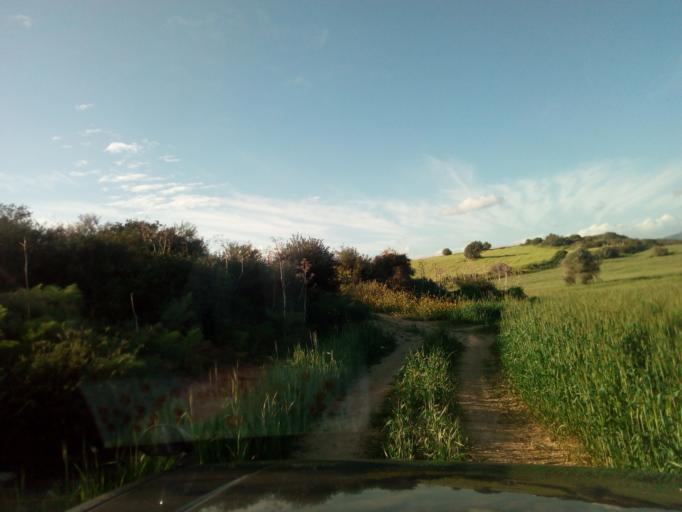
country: CY
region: Larnaka
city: Kofinou
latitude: 34.8002
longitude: 33.4225
